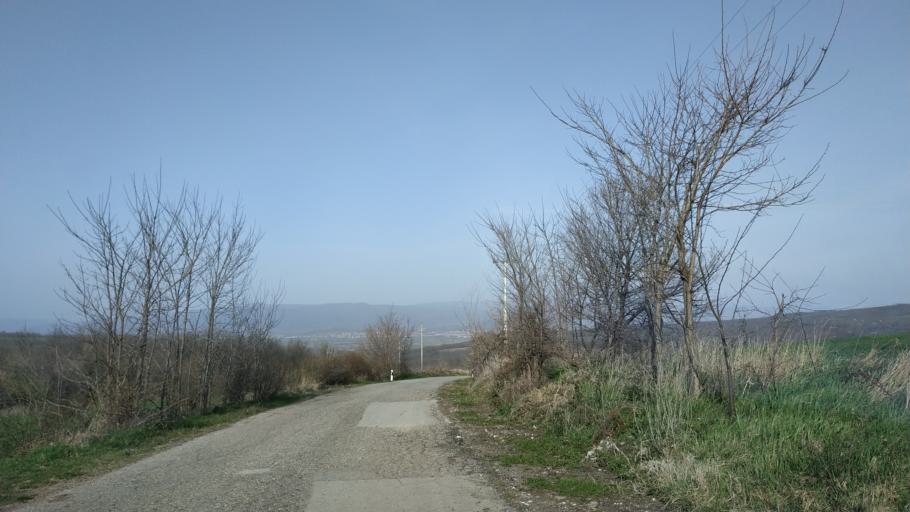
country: RS
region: Central Serbia
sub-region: Nisavski Okrug
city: Aleksinac
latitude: 43.5002
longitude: 21.6344
